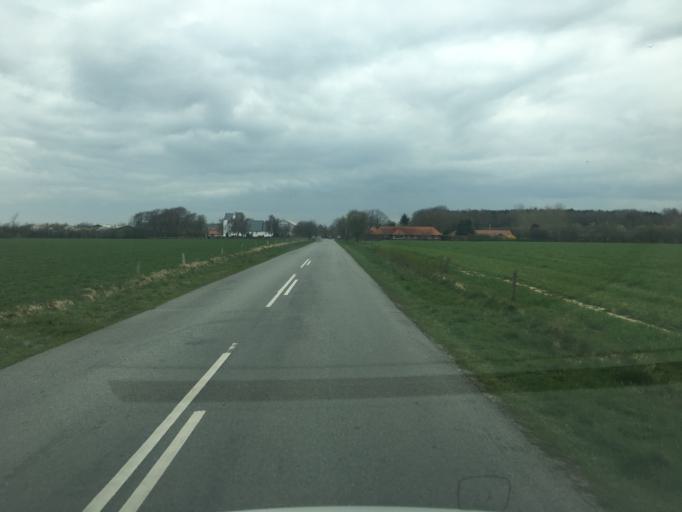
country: DK
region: South Denmark
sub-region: Tonder Kommune
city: Toftlund
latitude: 55.0550
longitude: 9.1067
